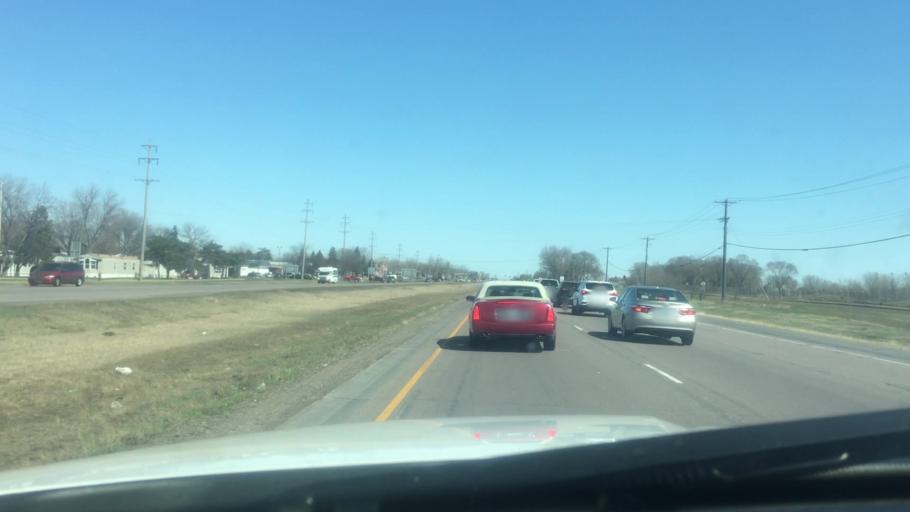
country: US
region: Minnesota
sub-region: Anoka County
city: Blaine
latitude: 45.1435
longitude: -93.2351
